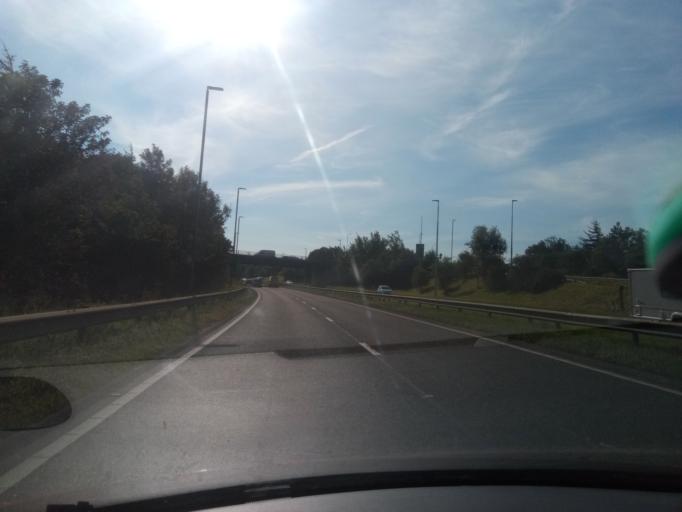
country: GB
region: England
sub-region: County Durham
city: Hawthorn
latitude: 54.8063
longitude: -1.3593
